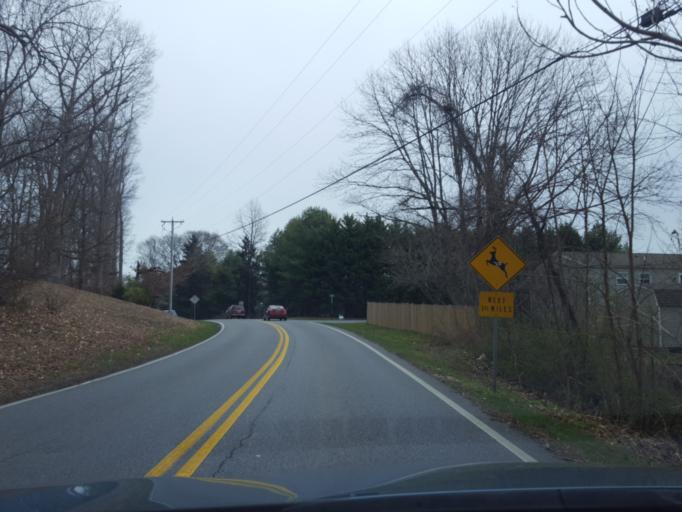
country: US
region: Maryland
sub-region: Calvert County
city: Owings
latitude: 38.7110
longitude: -76.5682
